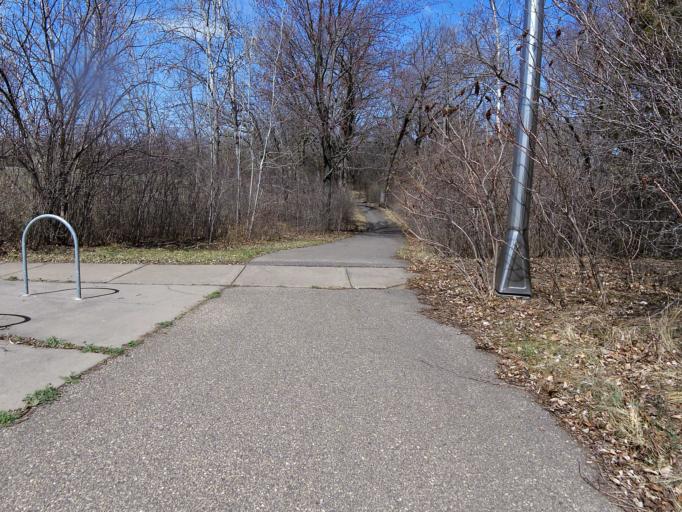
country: US
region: Minnesota
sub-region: Washington County
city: Lakeland
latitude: 44.9516
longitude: -92.8197
